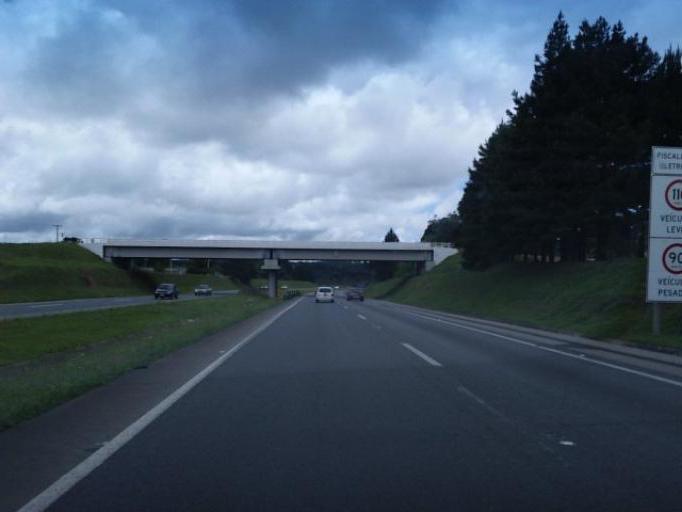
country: BR
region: Parana
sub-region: Piraquara
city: Piraquara
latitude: -25.4861
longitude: -49.1093
